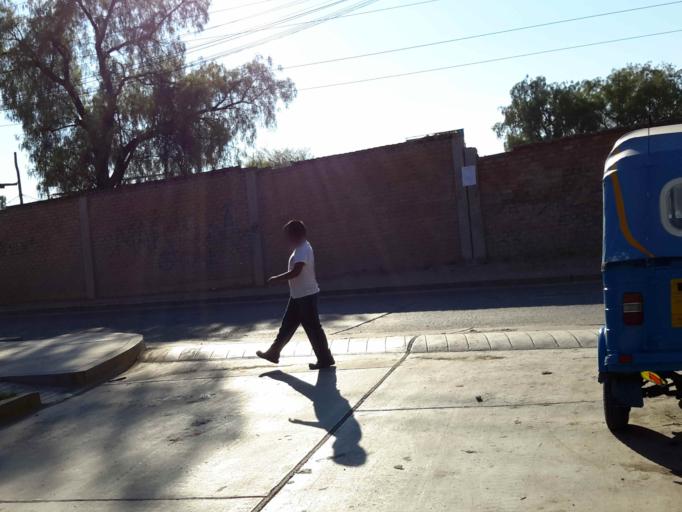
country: PE
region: Ayacucho
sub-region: Provincia de Huamanga
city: Ayacucho
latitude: -13.1519
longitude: -74.2213
